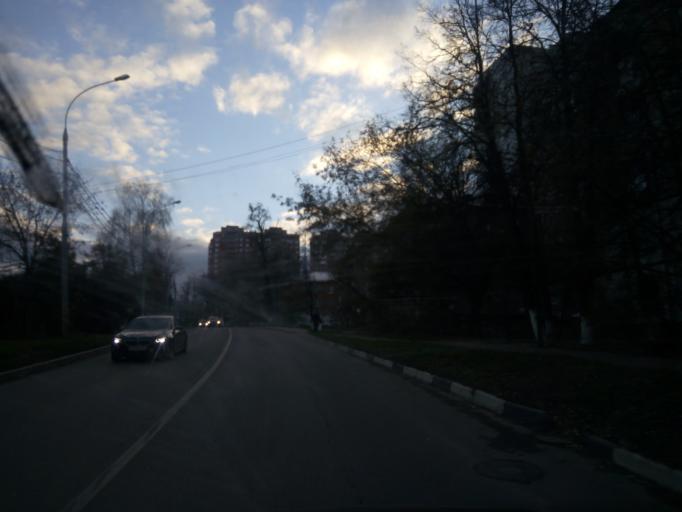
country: RU
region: Moskovskaya
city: Skhodnya
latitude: 55.9601
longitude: 37.3067
